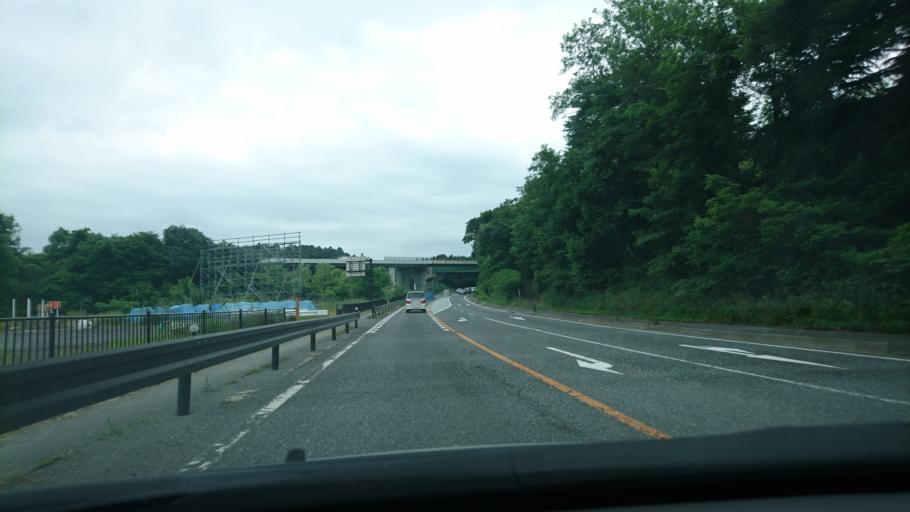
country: JP
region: Miyagi
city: Furukawa
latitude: 38.7207
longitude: 141.0243
